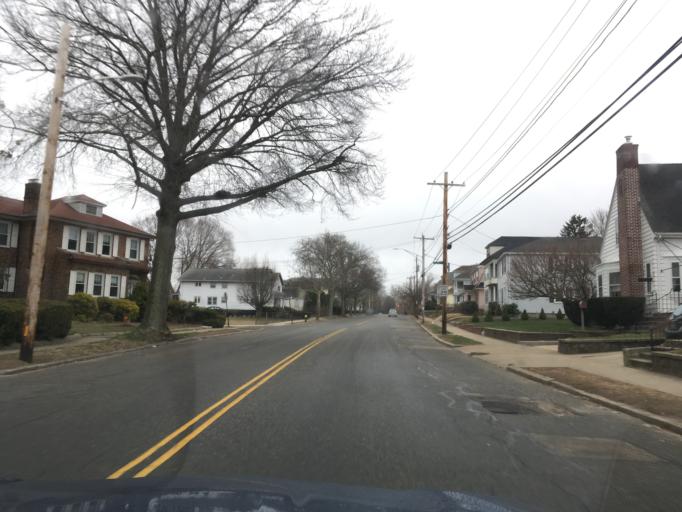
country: US
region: Rhode Island
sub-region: Providence County
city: North Providence
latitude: 41.8355
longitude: -71.4505
